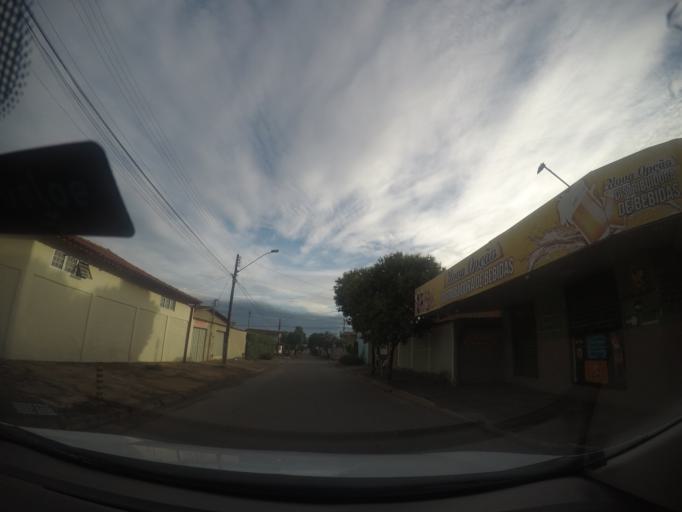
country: BR
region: Goias
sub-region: Goiania
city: Goiania
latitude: -16.6440
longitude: -49.3214
